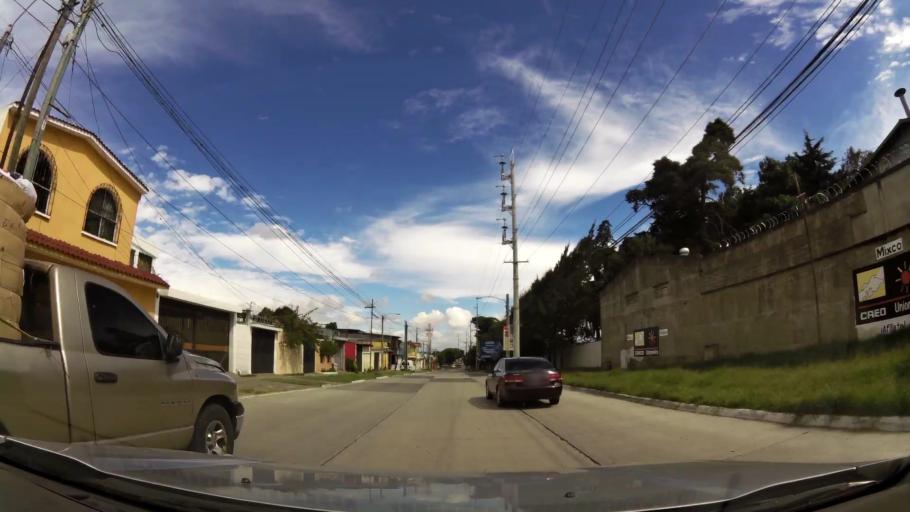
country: GT
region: Guatemala
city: Mixco
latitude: 14.6363
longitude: -90.5869
